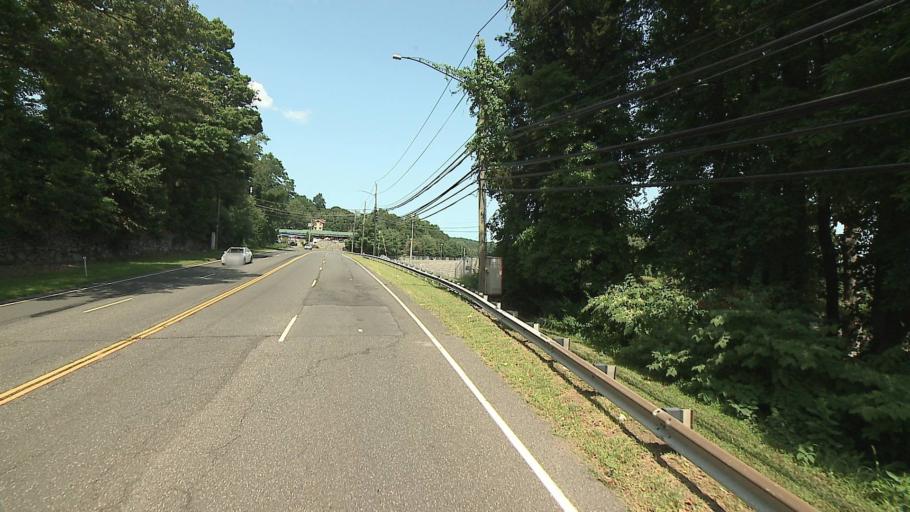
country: US
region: Connecticut
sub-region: New Haven County
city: City of Milford (balance)
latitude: 41.2511
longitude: -73.1006
